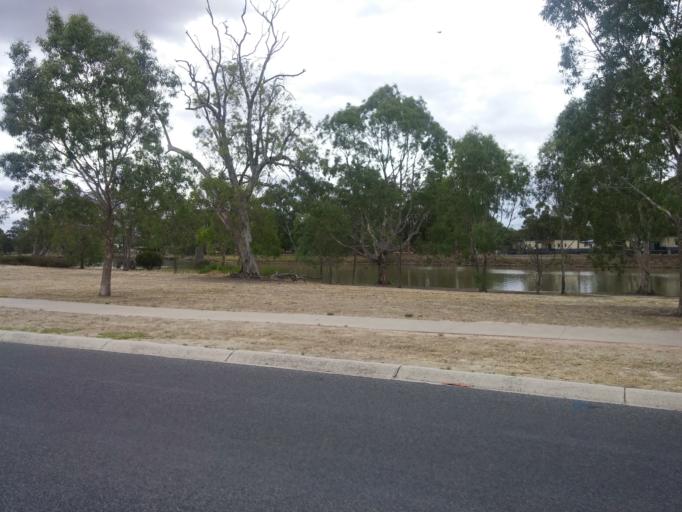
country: AU
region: Victoria
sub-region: Horsham
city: Horsham
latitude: -36.7252
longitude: 142.1987
